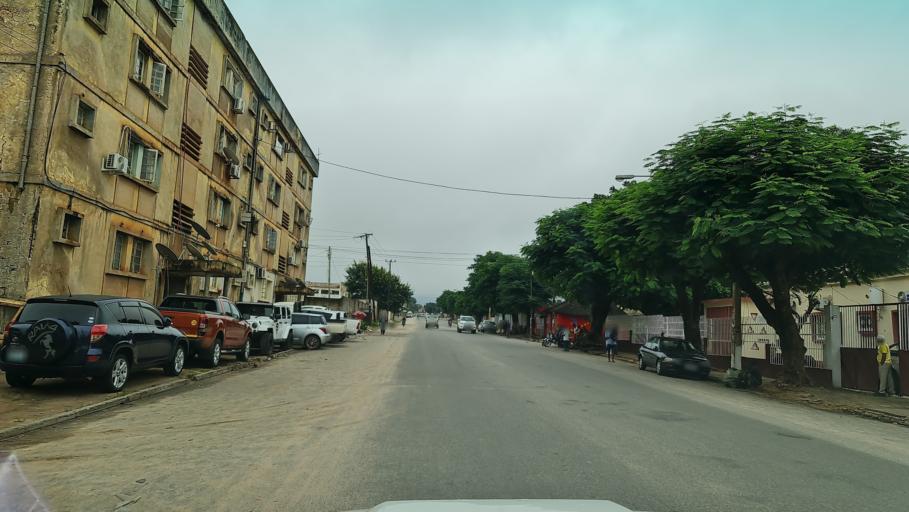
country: MZ
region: Nampula
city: Nampula
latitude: -15.1297
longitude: 39.2650
